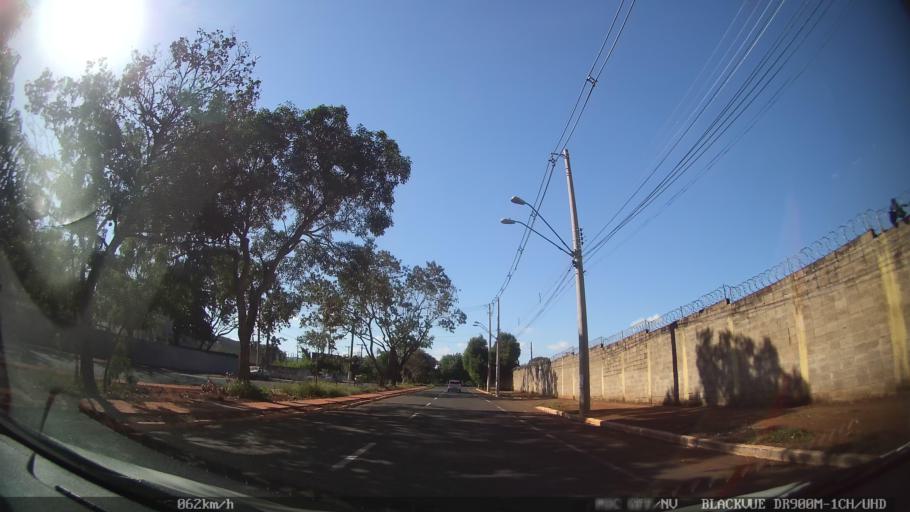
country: BR
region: Sao Paulo
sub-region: Ribeirao Preto
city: Ribeirao Preto
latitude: -21.1534
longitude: -47.7817
